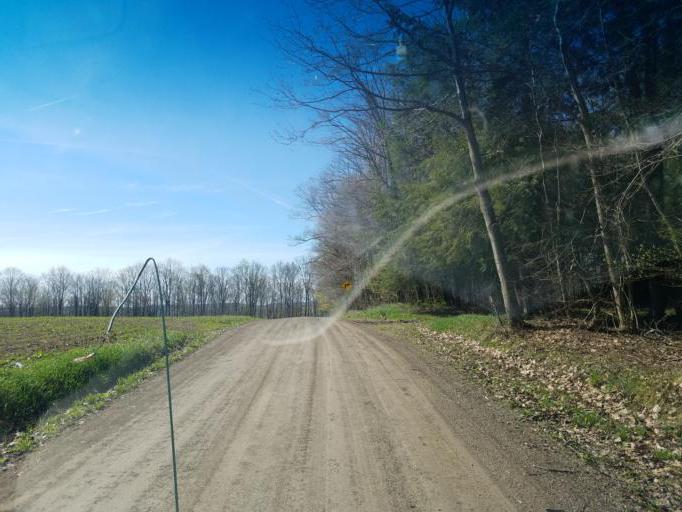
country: US
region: New York
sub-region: Allegany County
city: Andover
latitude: 41.9767
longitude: -77.7858
